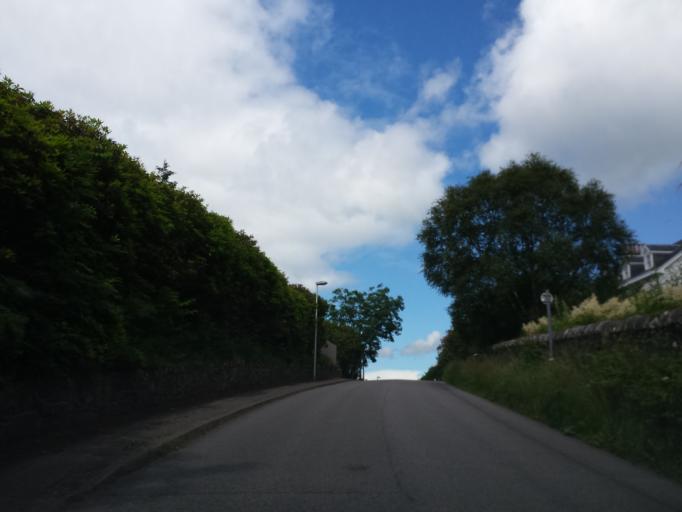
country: GB
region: Scotland
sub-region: Highland
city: Ullapool
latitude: 57.7136
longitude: -5.6801
